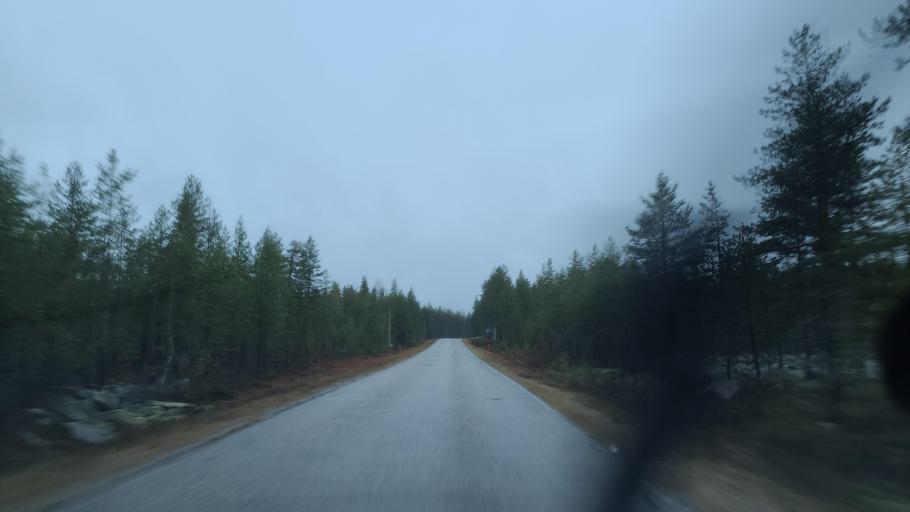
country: FI
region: Lapland
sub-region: Kemi-Tornio
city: Simo
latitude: 65.9158
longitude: 25.2006
